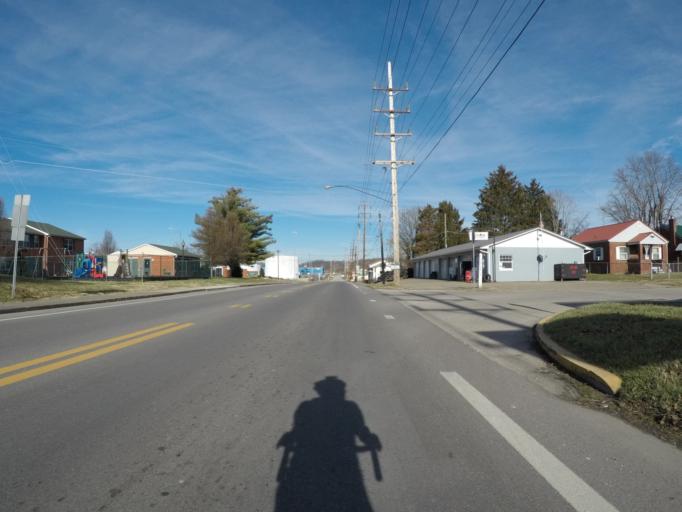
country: US
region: West Virginia
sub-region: Wayne County
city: Kenova
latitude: 38.4030
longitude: -82.5877
